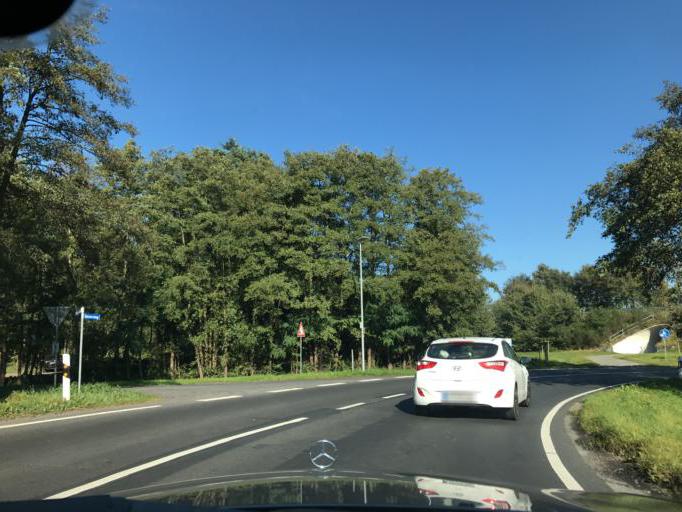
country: DE
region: Lower Saxony
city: Papenburg
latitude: 53.0811
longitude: 7.3769
